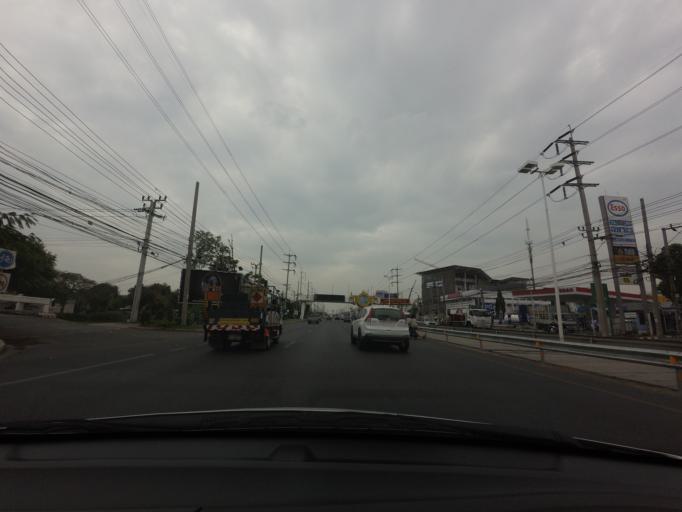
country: TH
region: Samut Prakan
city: Samut Prakan
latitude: 13.5456
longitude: 100.6184
